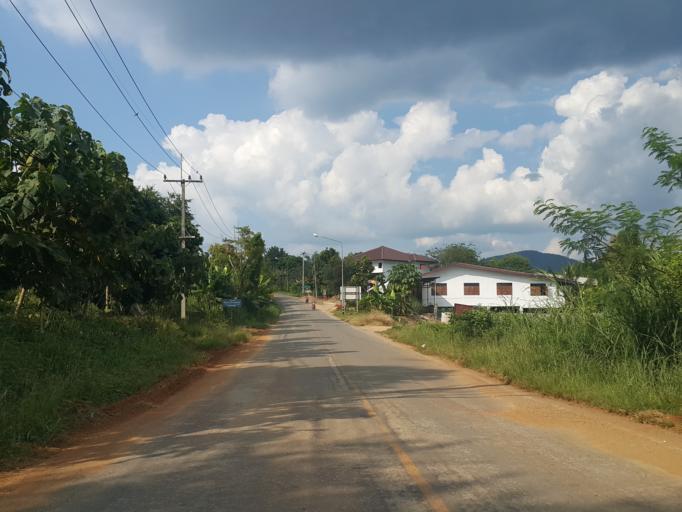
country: TH
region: Chiang Mai
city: Mae Chaem
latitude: 18.5183
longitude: 98.3627
